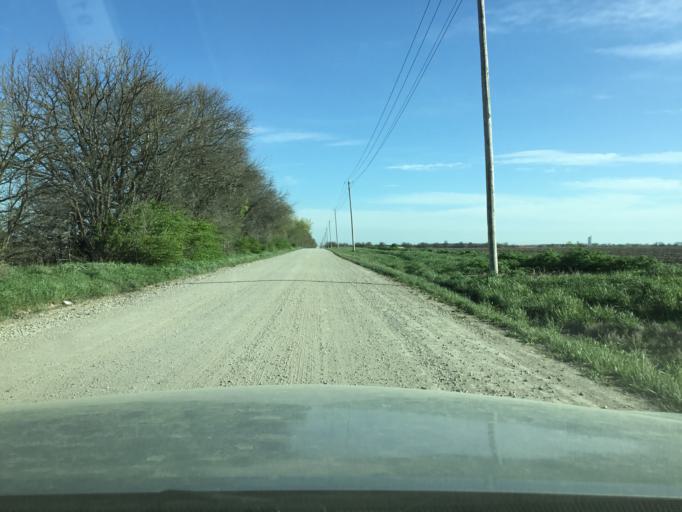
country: US
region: Kansas
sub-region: Neosho County
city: Chanute
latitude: 37.6464
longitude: -95.4893
